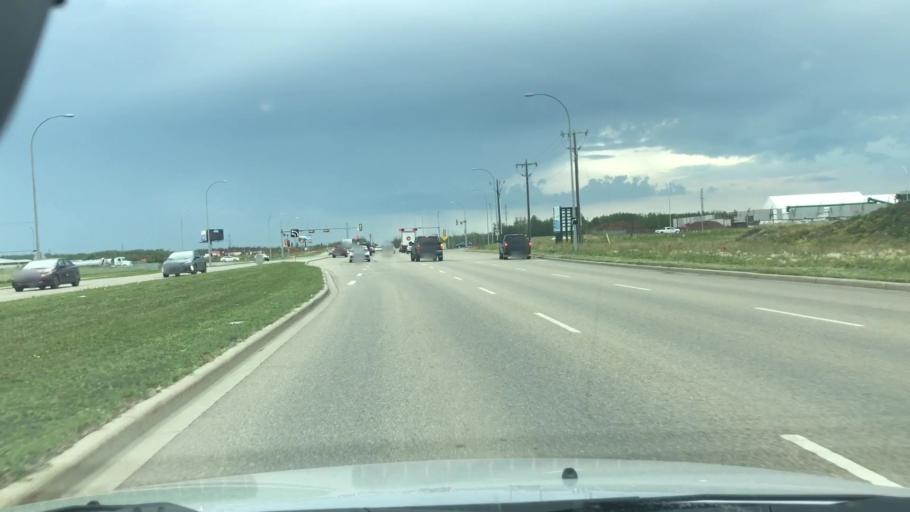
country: CA
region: Alberta
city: St. Albert
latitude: 53.5994
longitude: -113.6117
